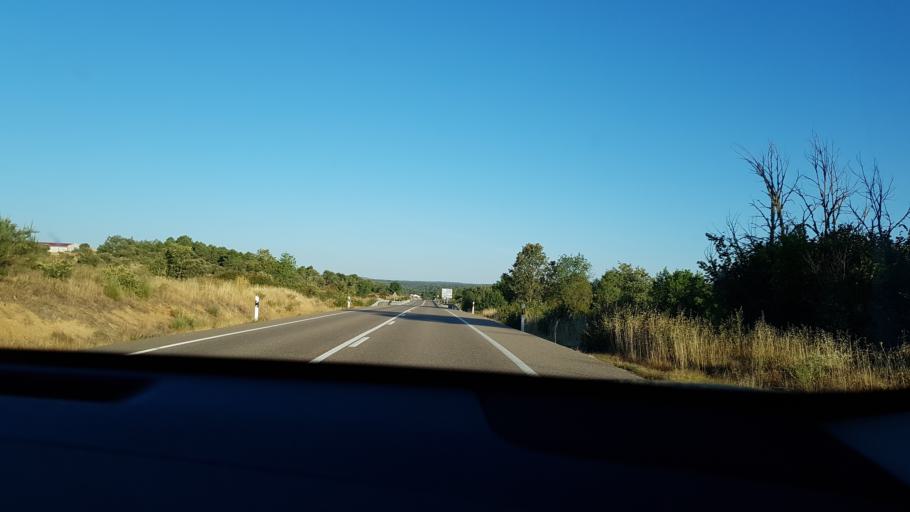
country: ES
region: Castille and Leon
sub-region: Provincia de Zamora
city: Samir de los Canos
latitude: 41.6537
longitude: -6.1801
